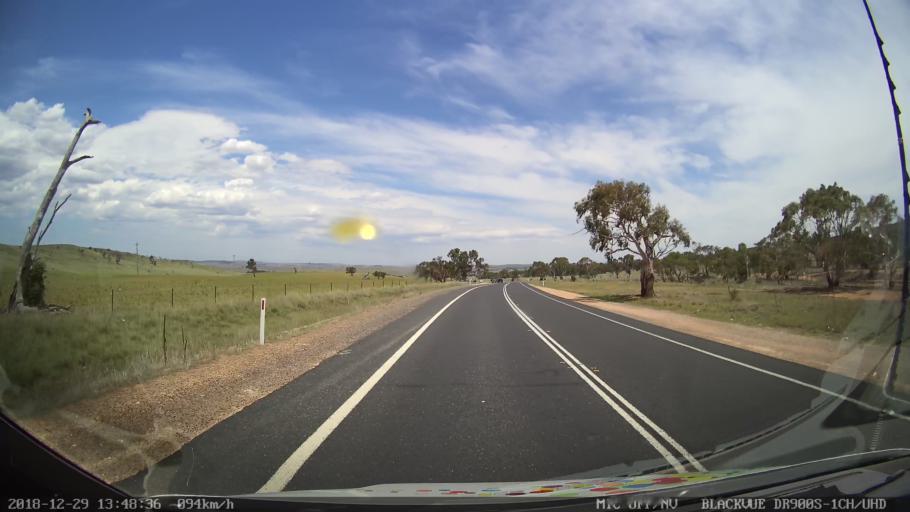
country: AU
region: New South Wales
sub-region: Cooma-Monaro
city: Cooma
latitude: -36.1424
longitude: 149.1486
